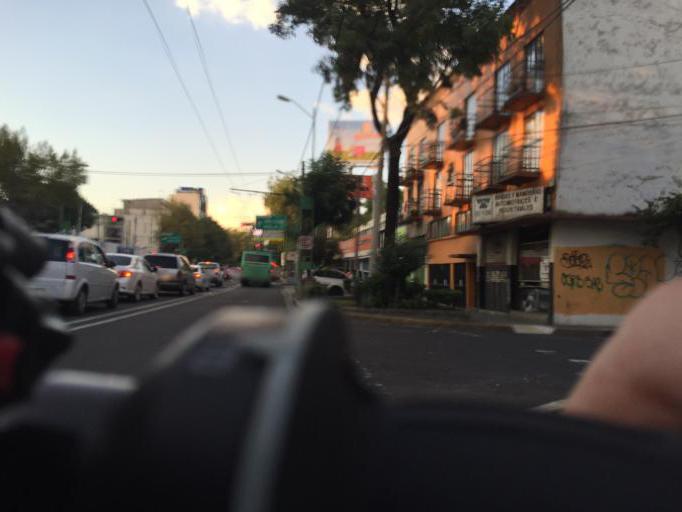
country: MX
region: Mexico City
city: Colonia Nativitas
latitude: 19.3833
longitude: -99.1475
